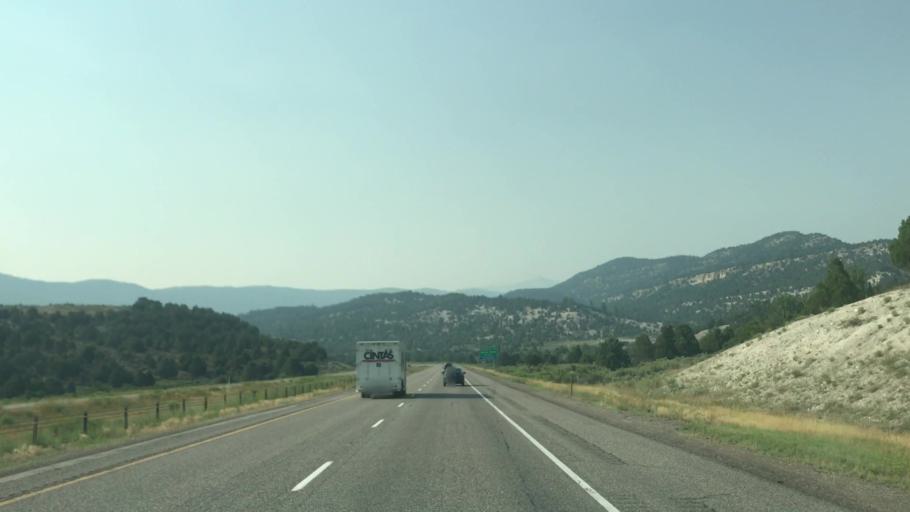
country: US
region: Utah
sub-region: Sevier County
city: Salina
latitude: 38.8693
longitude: -111.5524
